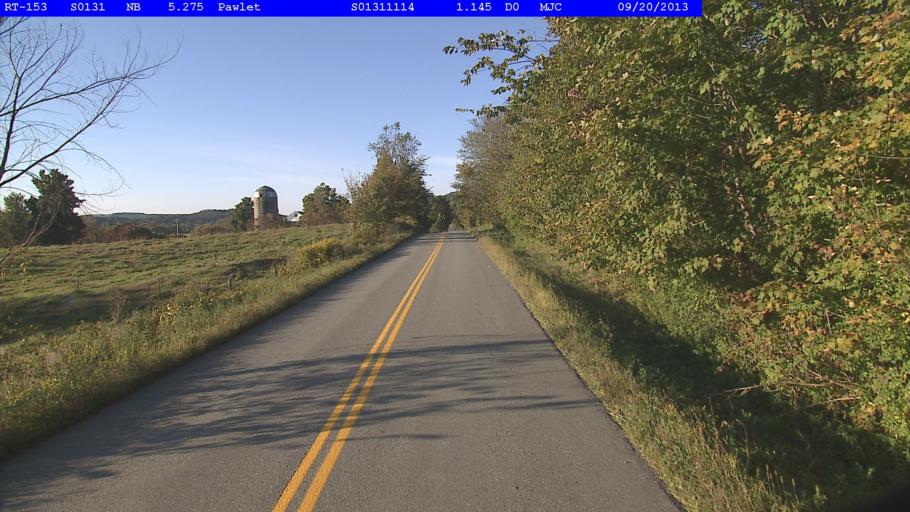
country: US
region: New York
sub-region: Washington County
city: Granville
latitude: 43.3304
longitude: -73.2435
